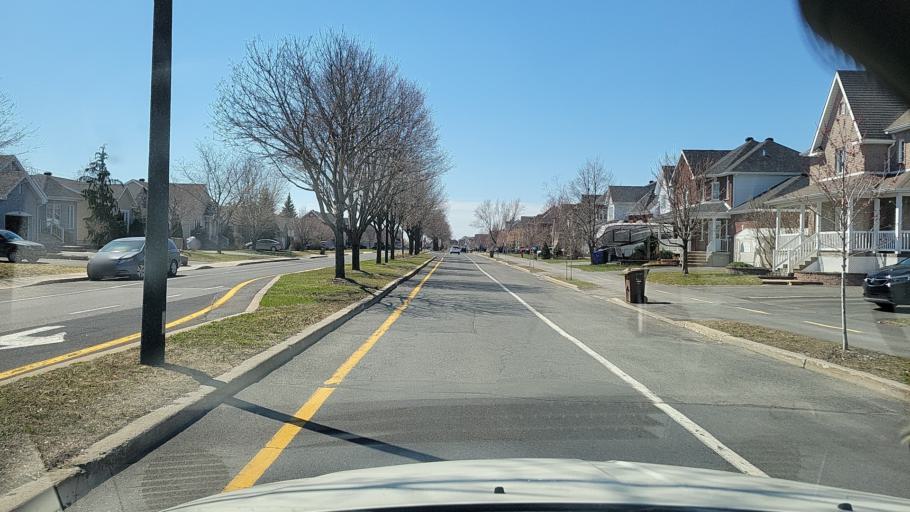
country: CA
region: Quebec
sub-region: Monteregie
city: Sainte-Julie
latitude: 45.5859
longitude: -73.3504
